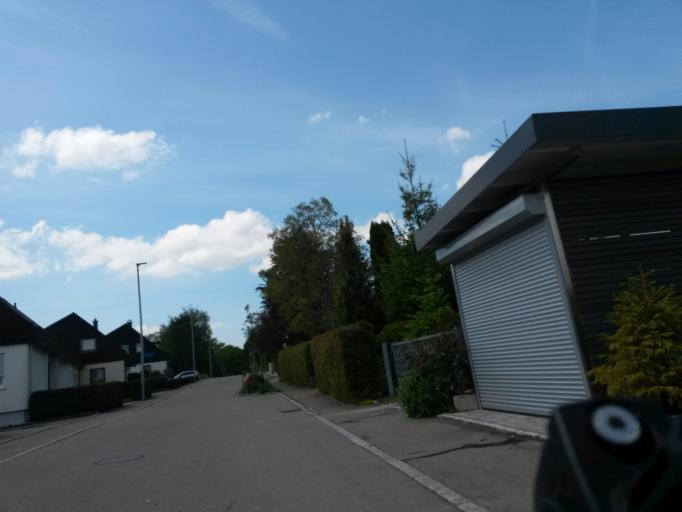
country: DE
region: Baden-Wuerttemberg
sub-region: Tuebingen Region
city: Bad Waldsee
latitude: 47.9123
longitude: 9.7503
